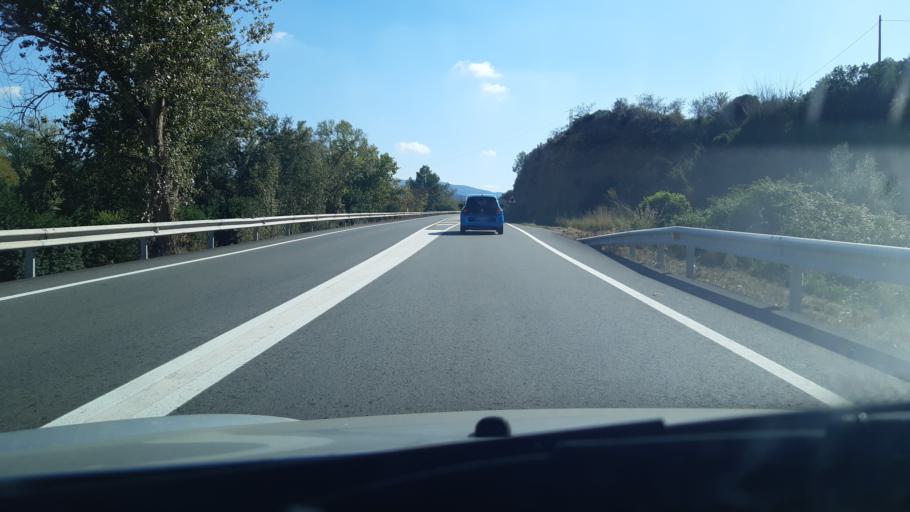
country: ES
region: Catalonia
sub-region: Provincia de Tarragona
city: Tortosa
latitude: 40.8587
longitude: 0.5108
